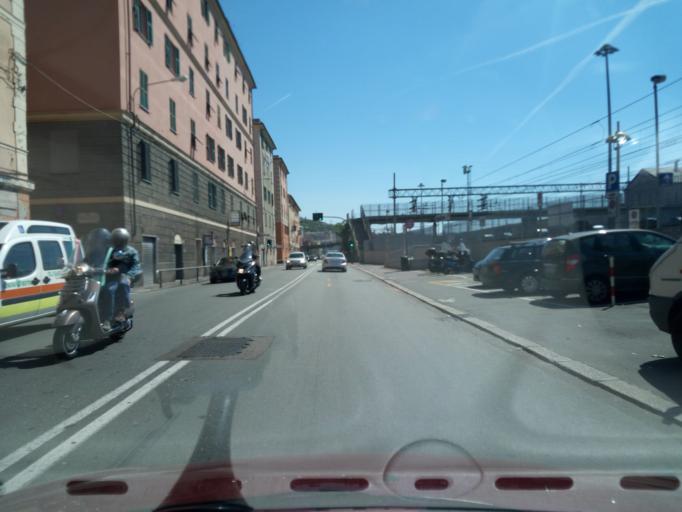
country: IT
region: Liguria
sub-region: Provincia di Genova
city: San Teodoro
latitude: 44.4223
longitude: 8.8490
